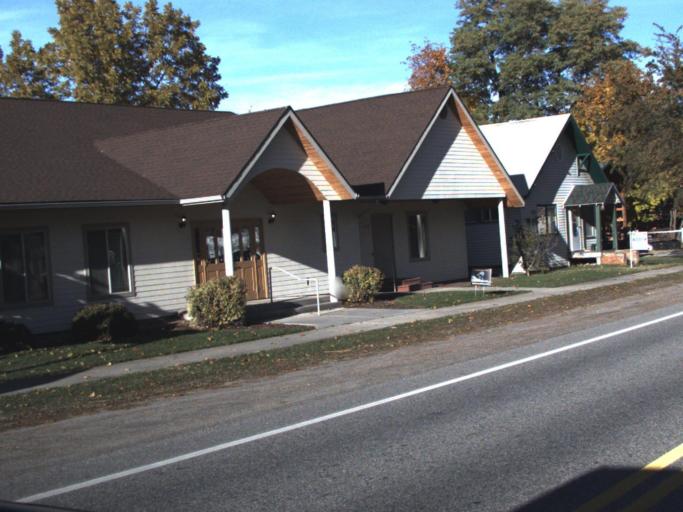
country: CA
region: British Columbia
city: Rossland
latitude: 48.9144
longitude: -117.7865
